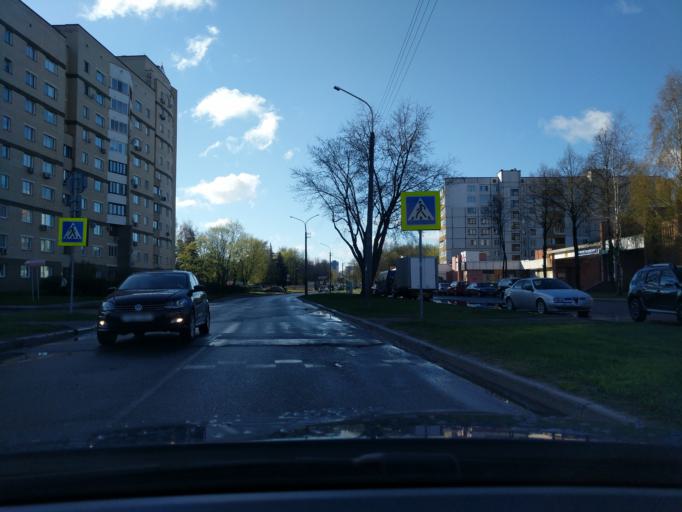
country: BY
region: Minsk
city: Novoye Medvezhino
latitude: 53.9012
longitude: 27.5052
